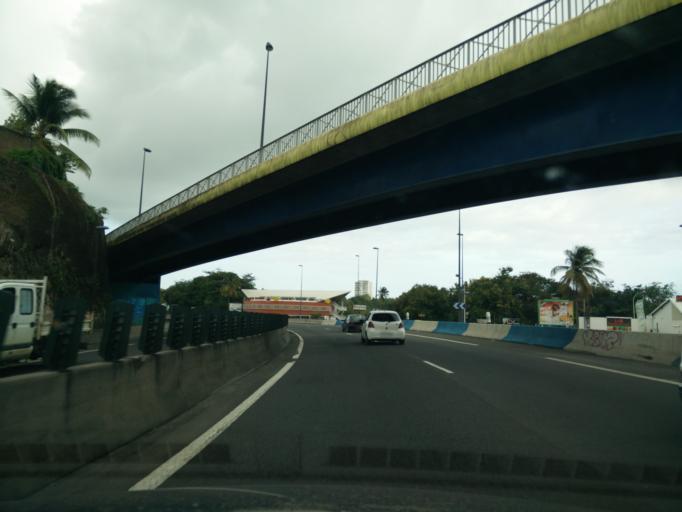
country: GP
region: Guadeloupe
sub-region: Guadeloupe
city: Pointe-a-Pitre
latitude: 16.2223
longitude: -61.5230
